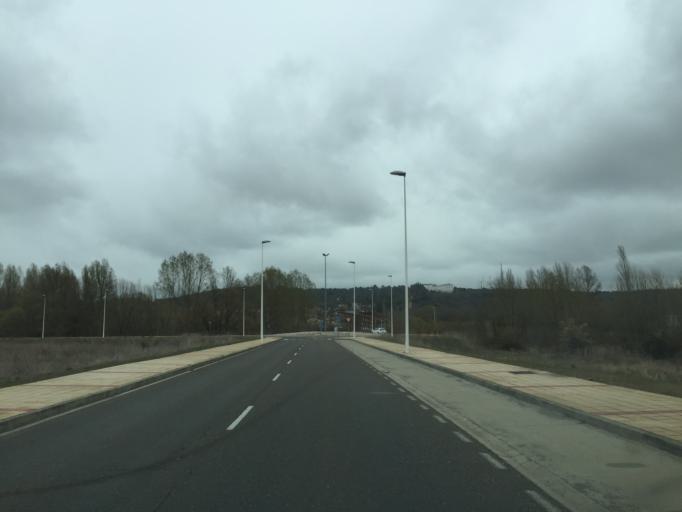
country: ES
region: Castille and Leon
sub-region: Provincia de Leon
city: San Andres del Rabanedo
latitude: 42.6366
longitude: -5.6104
